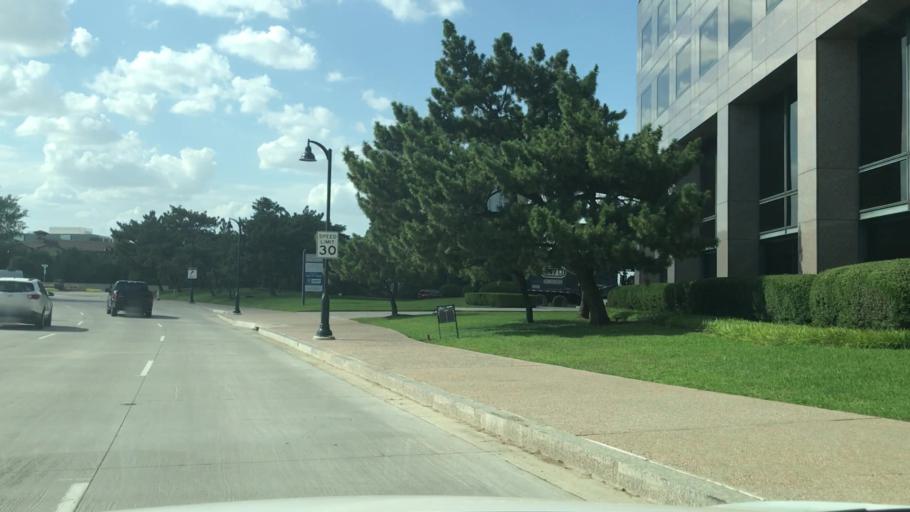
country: US
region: Texas
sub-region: Dallas County
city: Irving
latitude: 32.8698
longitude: -96.9410
